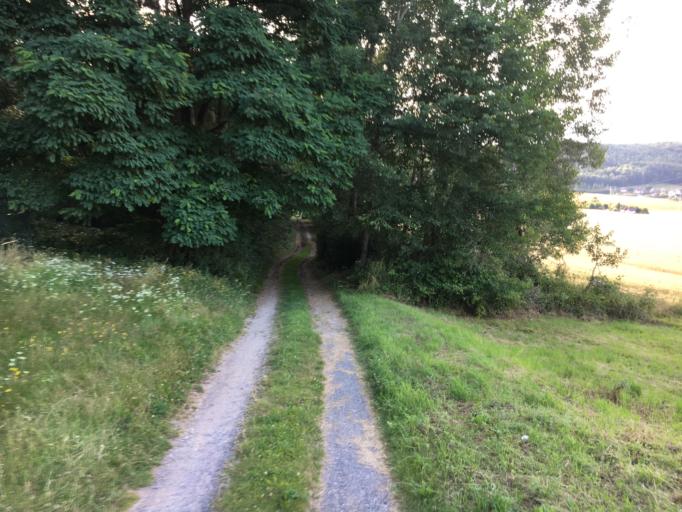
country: DE
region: Thuringia
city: Stadtlengsfeld
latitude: 50.8131
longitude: 10.1209
